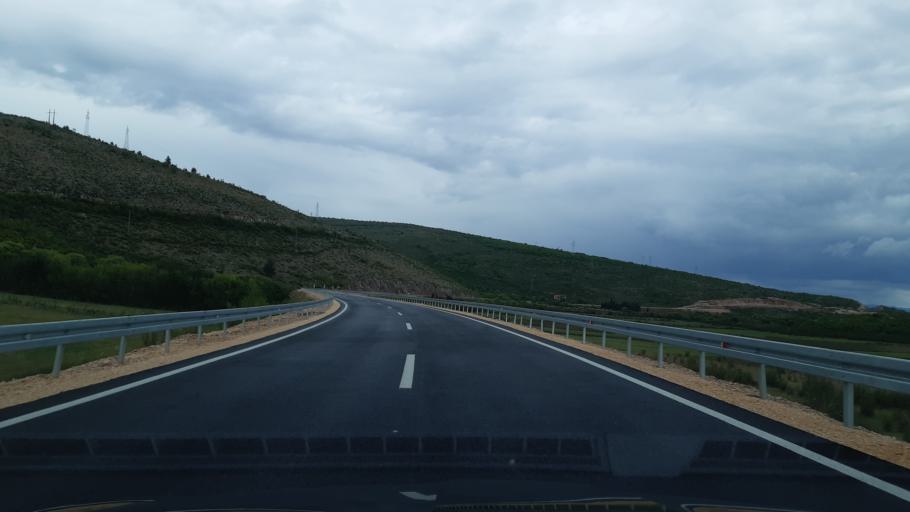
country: BA
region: Federation of Bosnia and Herzegovina
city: Ilici
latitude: 43.3323
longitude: 17.7227
